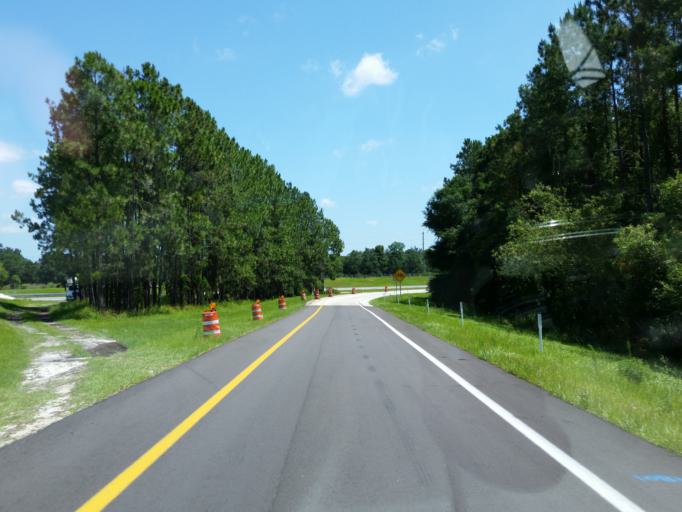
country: US
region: Florida
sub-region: Hillsborough County
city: Temple Terrace
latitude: 28.0526
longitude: -82.3506
